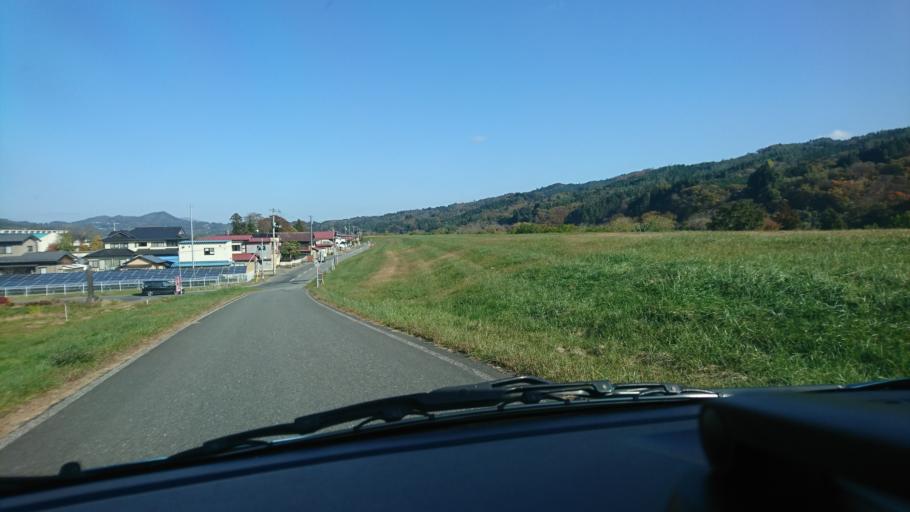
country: JP
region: Iwate
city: Ichinoseki
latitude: 38.8297
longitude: 141.2530
